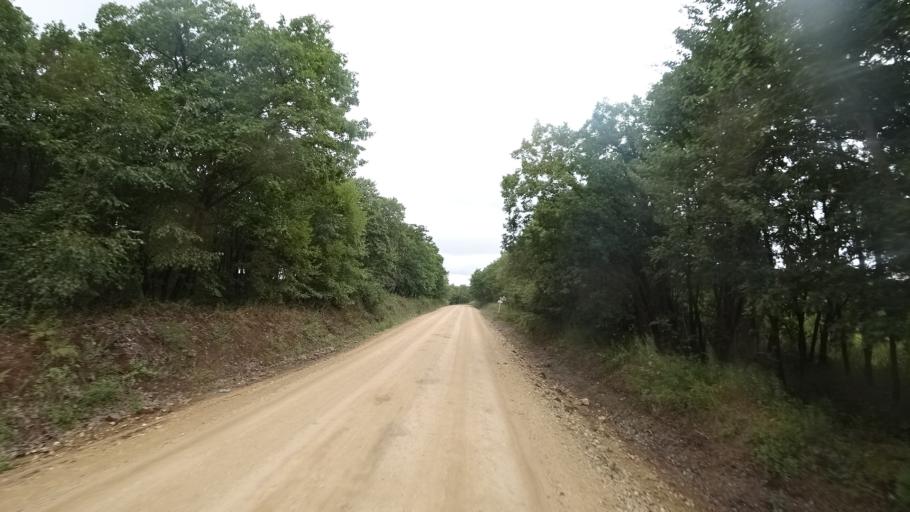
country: RU
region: Primorskiy
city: Chernigovka
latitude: 44.3425
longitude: 132.6187
